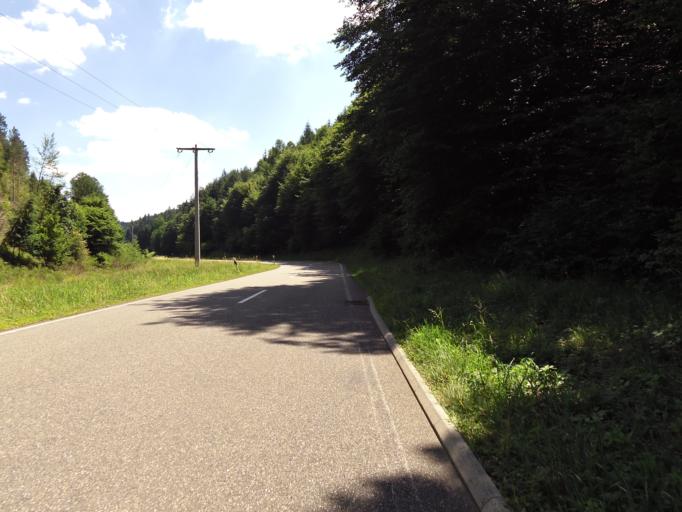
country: DE
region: Rheinland-Pfalz
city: Waldleiningen
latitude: 49.3496
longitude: 7.8546
